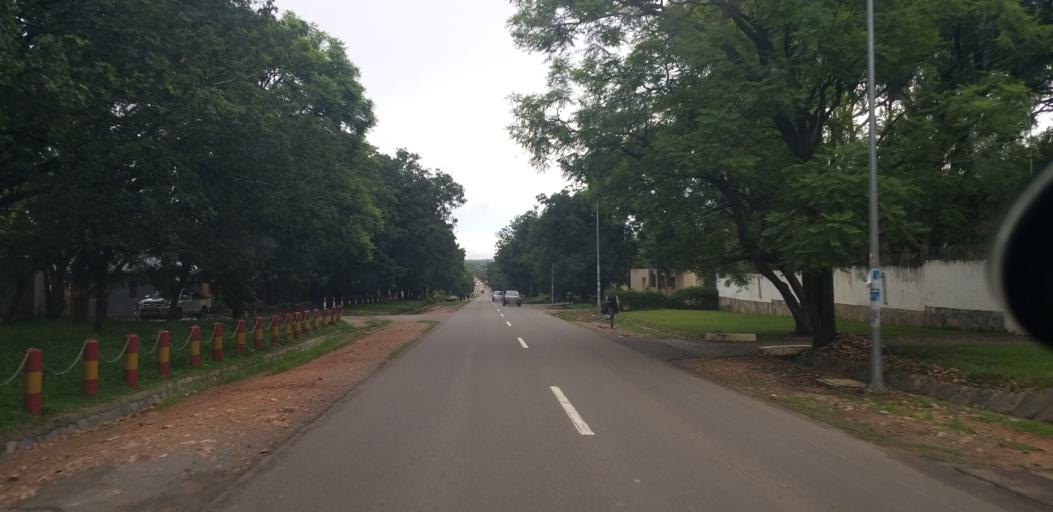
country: ZM
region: Lusaka
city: Lusaka
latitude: -15.4331
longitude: 28.3487
